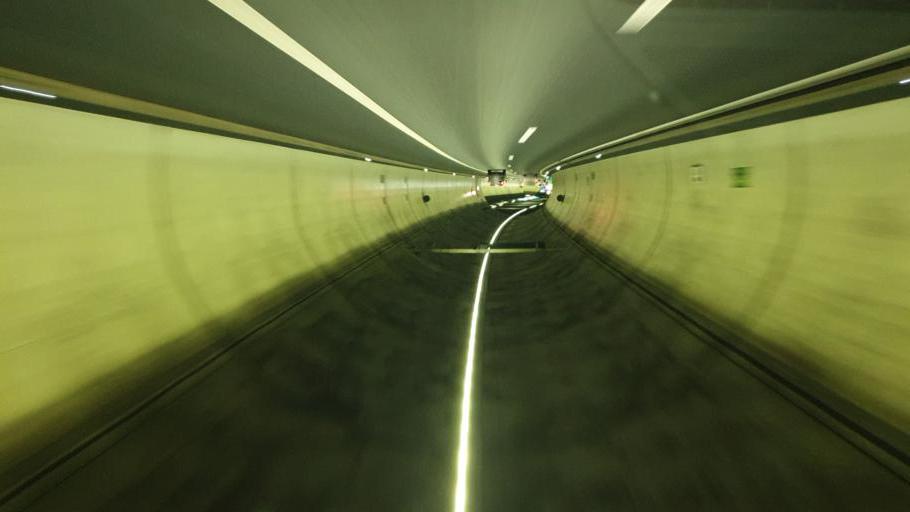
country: CH
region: Zurich
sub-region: Bezirk Dietikon
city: Birmensdorf
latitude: 47.3522
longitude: 8.4250
